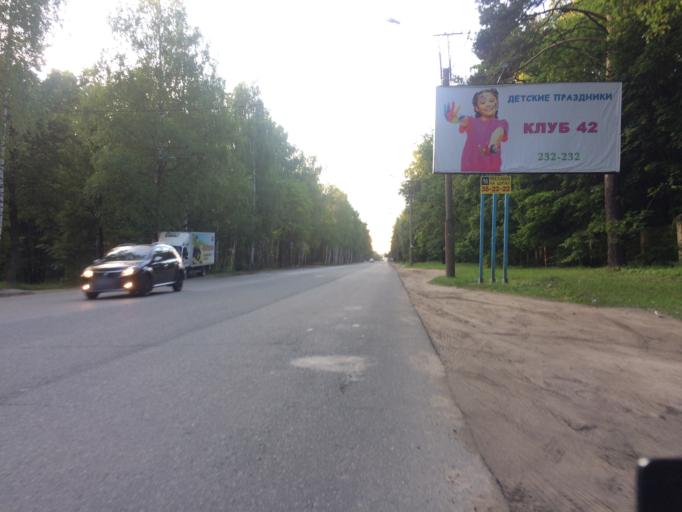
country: RU
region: Mariy-El
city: Yoshkar-Ola
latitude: 56.6216
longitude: 47.9555
